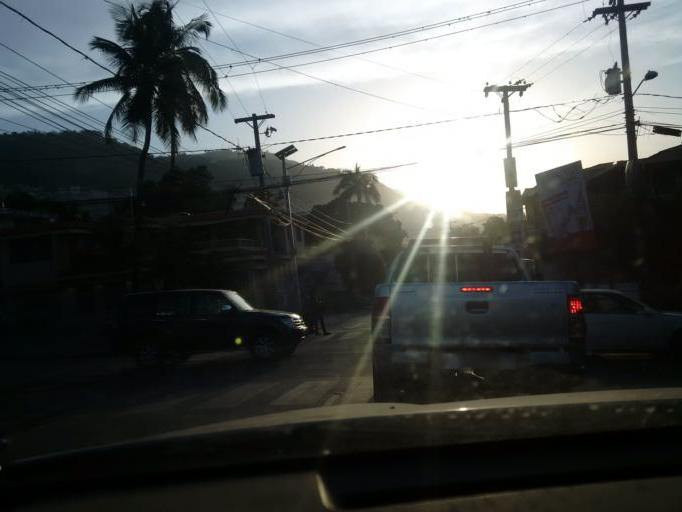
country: HT
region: Ouest
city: Petionville
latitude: 18.5128
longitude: -72.2885
